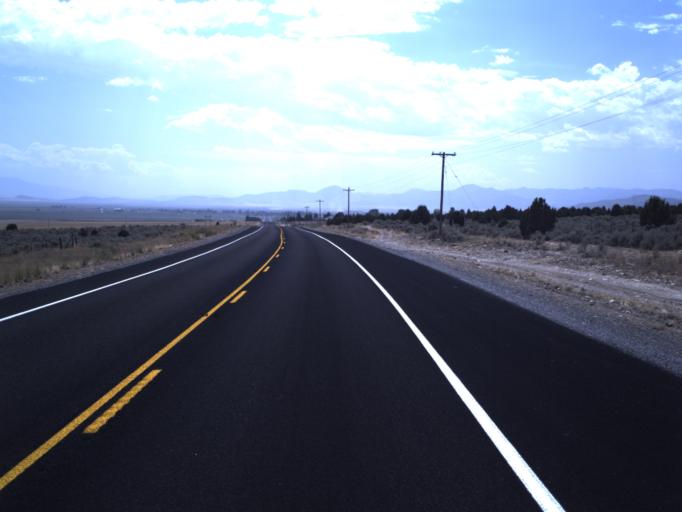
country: US
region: Utah
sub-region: Utah County
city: Eagle Mountain
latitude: 40.3137
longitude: -112.1024
